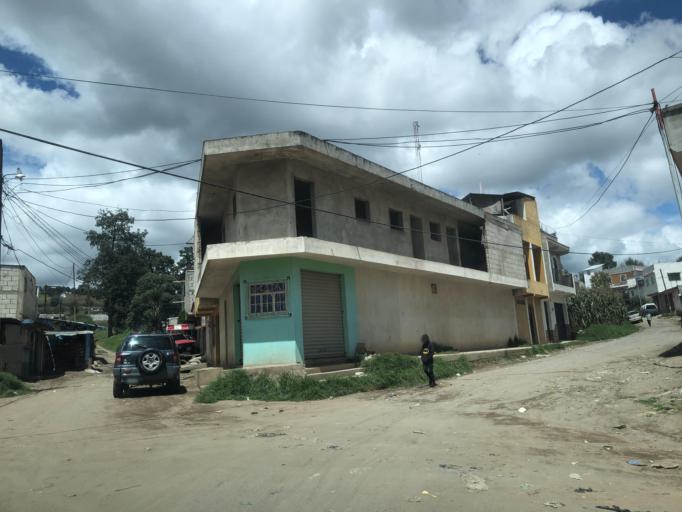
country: GT
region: Quetzaltenango
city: Quetzaltenango
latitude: 14.8384
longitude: -91.5461
